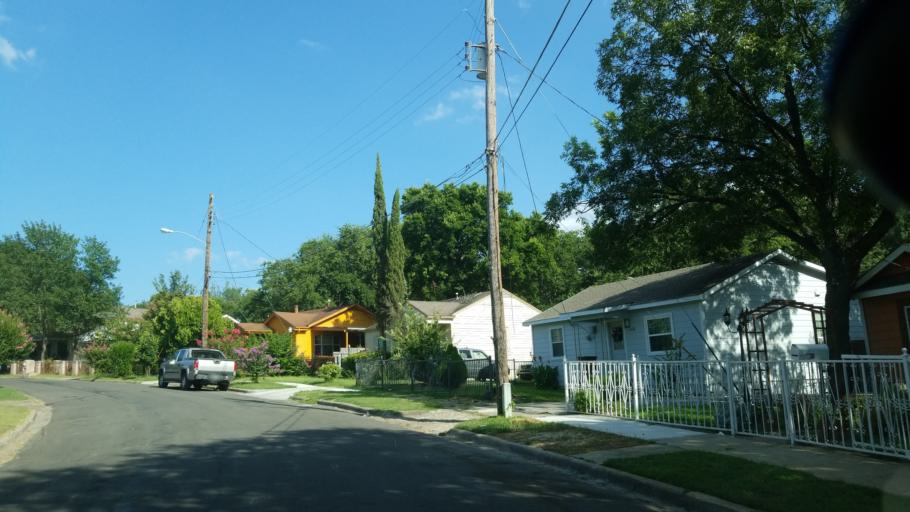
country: US
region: Texas
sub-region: Dallas County
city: Dallas
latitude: 32.7684
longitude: -96.7113
